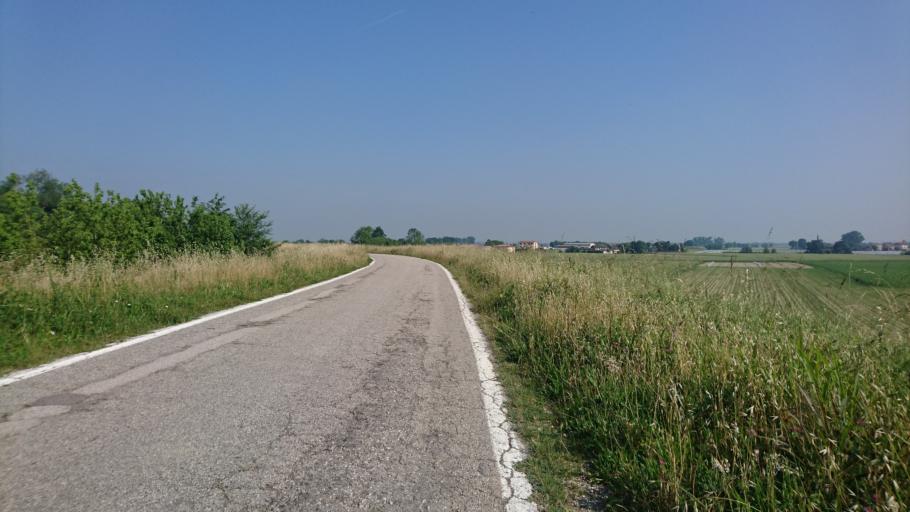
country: IT
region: Lombardy
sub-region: Provincia di Mantova
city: Borgofranco sul Po
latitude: 45.0545
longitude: 11.2247
